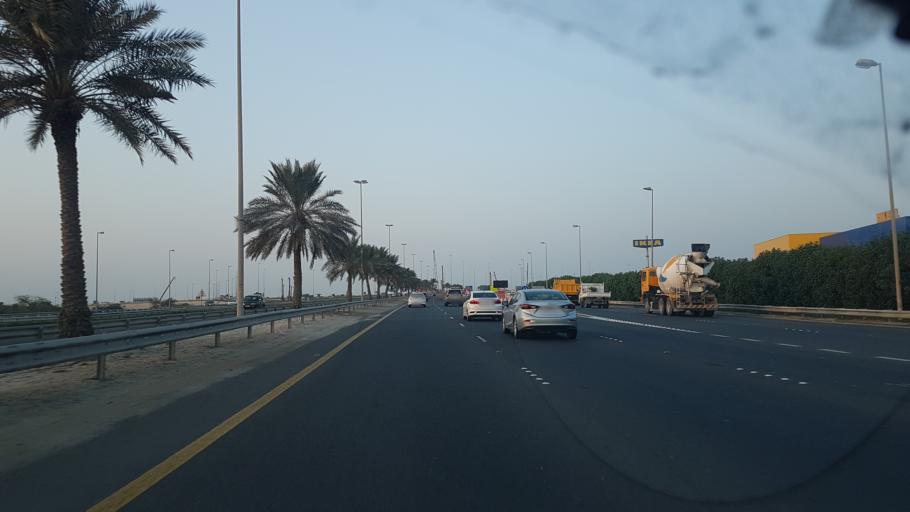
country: BH
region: Northern
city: Madinat `Isa
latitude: 26.1773
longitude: 50.5024
